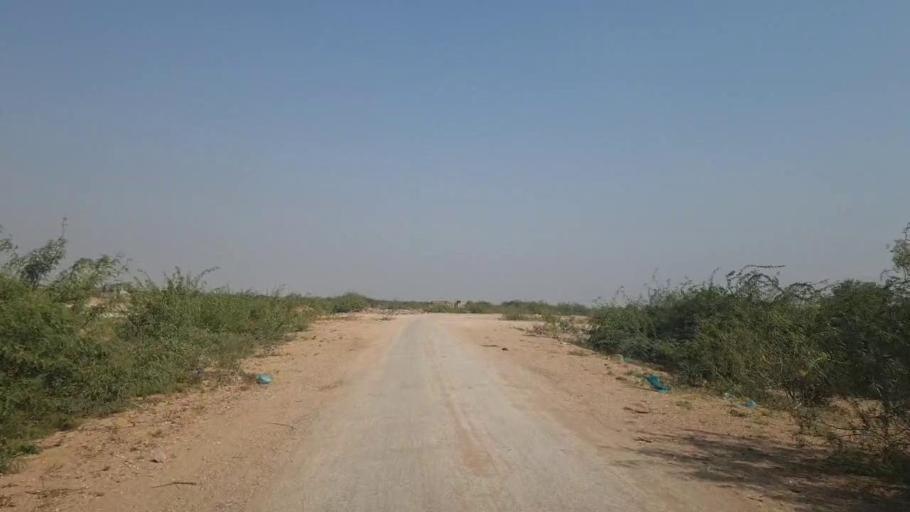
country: PK
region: Sindh
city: Jamshoro
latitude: 25.5349
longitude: 68.3407
